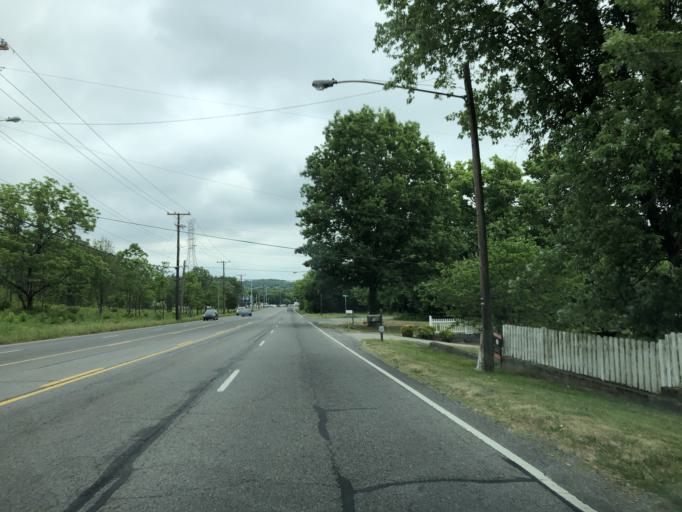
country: US
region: Tennessee
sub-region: Davidson County
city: Goodlettsville
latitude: 36.2837
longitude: -86.7472
